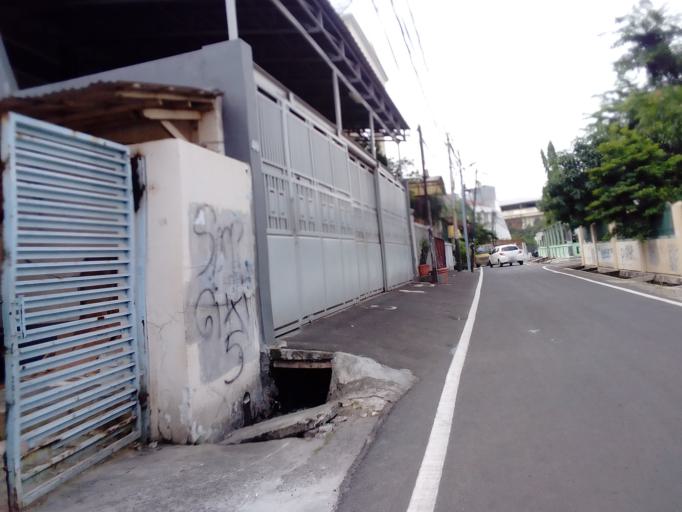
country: ID
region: Jakarta Raya
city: Jakarta
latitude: -6.1773
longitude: 106.8091
